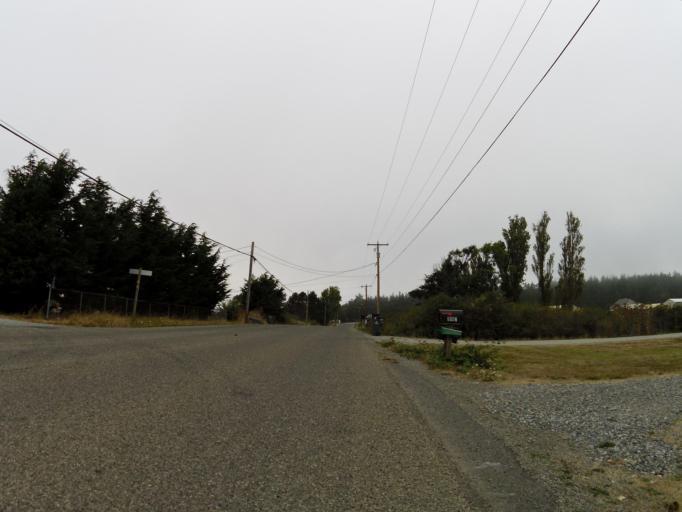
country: US
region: Washington
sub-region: Island County
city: Ault Field
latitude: 48.3048
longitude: -122.7130
